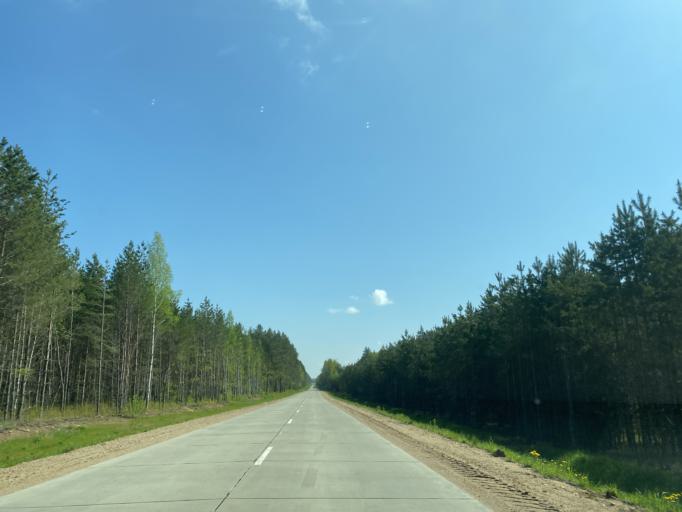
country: BY
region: Minsk
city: Horad Barysaw
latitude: 54.1658
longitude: 28.5045
